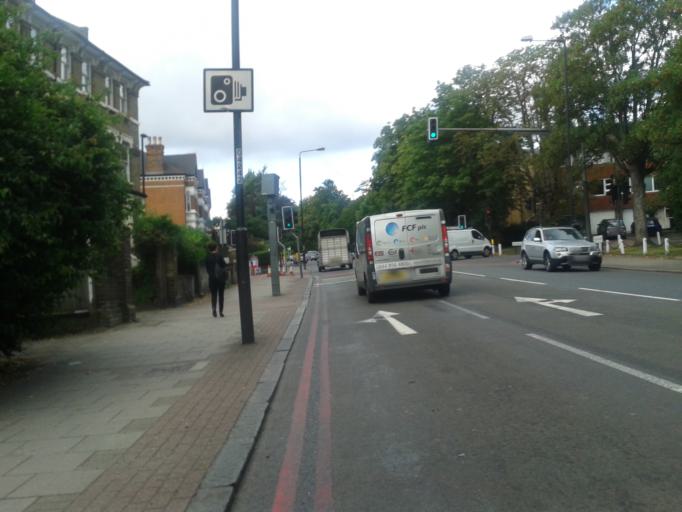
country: GB
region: England
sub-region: Greater London
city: Brixton
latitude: 51.4406
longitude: -0.0954
